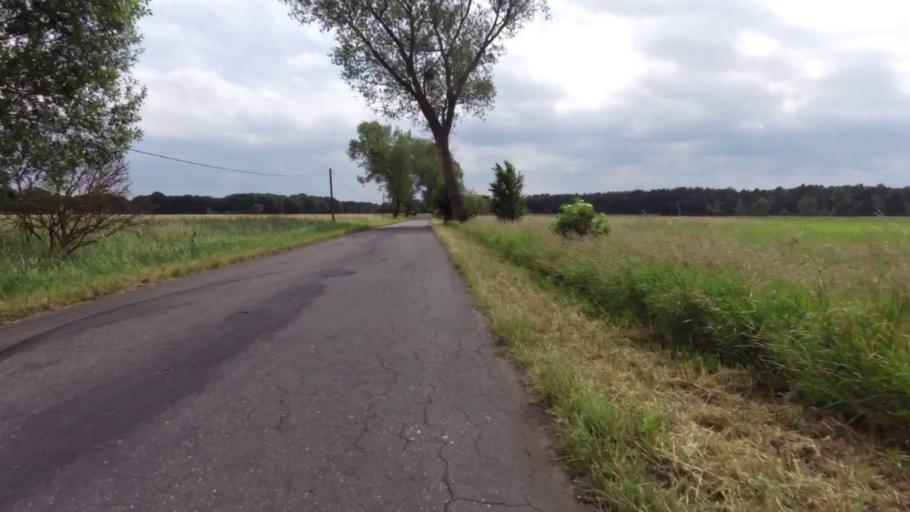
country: PL
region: West Pomeranian Voivodeship
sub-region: Powiat goleniowski
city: Stepnica
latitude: 53.7182
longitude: 14.5548
